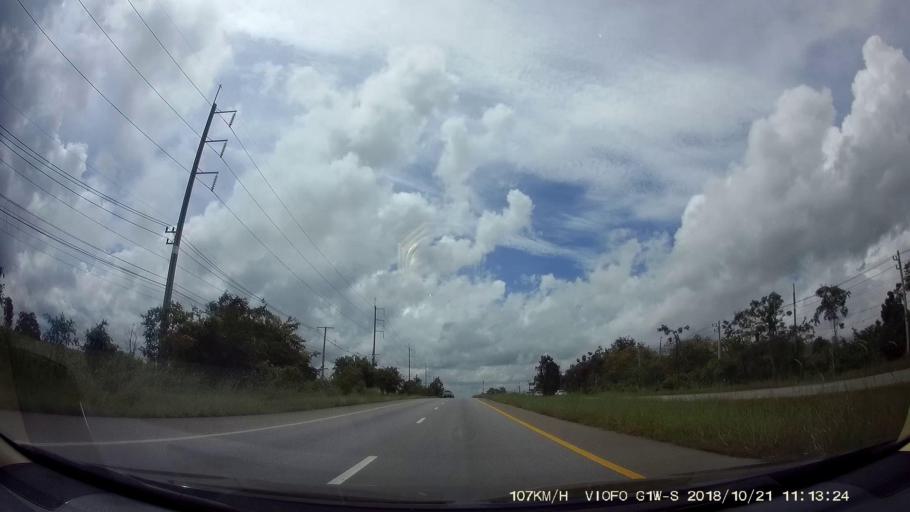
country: TH
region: Chaiyaphum
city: Khon Sawan
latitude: 15.9168
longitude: 102.1335
